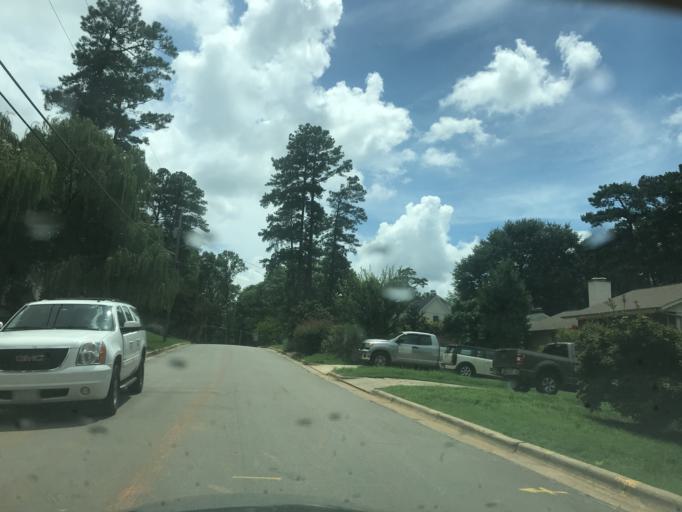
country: US
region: North Carolina
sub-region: Wake County
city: West Raleigh
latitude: 35.8128
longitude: -78.6367
